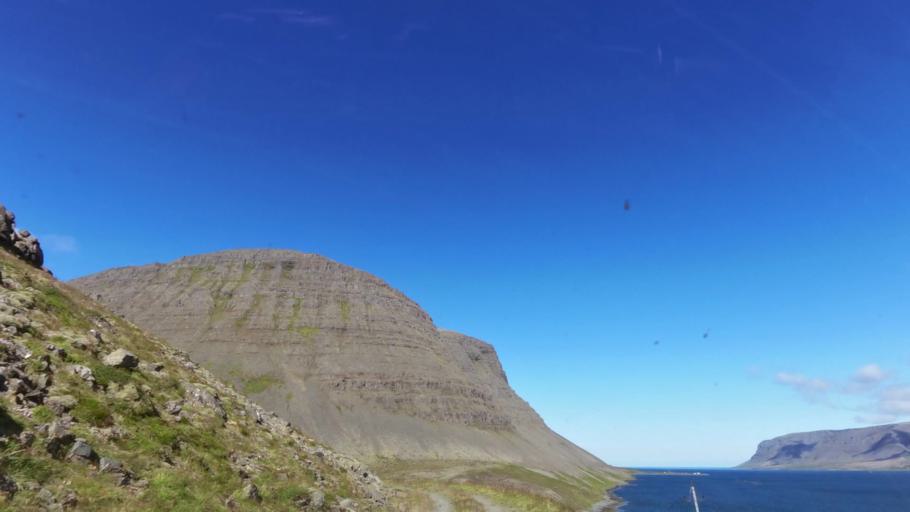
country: IS
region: West
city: Olafsvik
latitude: 65.6245
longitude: -23.8897
